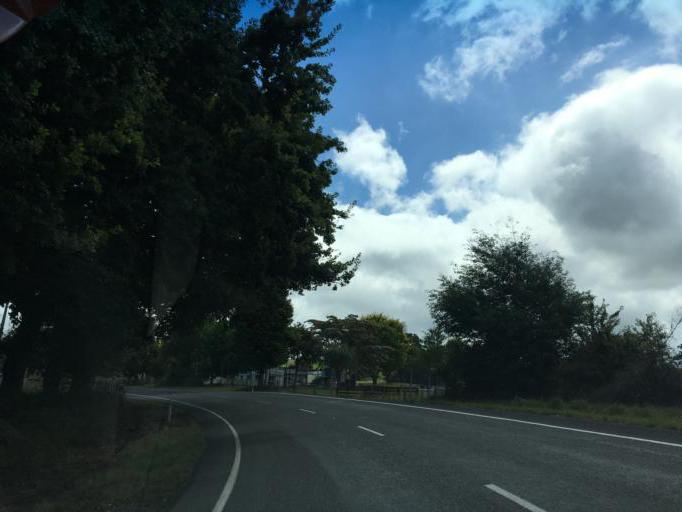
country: NZ
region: Hawke's Bay
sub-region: Wairoa District
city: Wairoa
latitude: -39.0627
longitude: 177.0368
